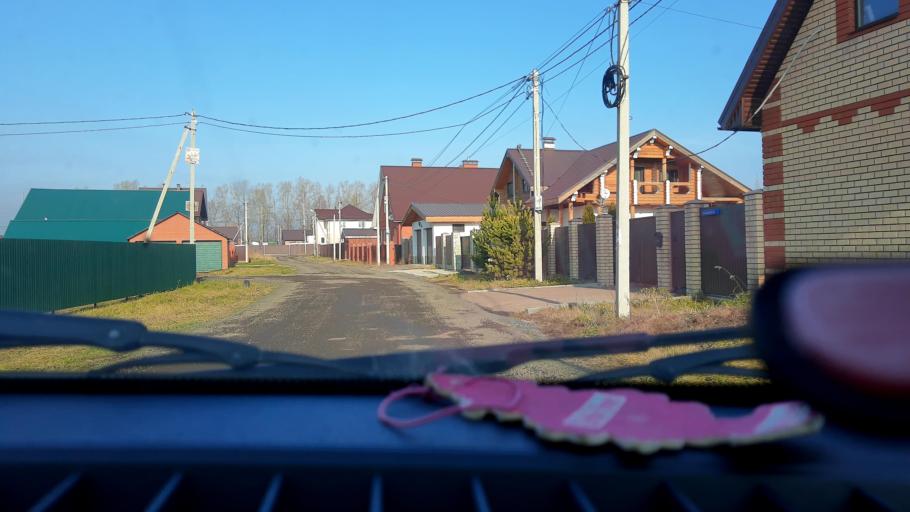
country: RU
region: Bashkortostan
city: Ufa
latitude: 54.6791
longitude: 56.0910
